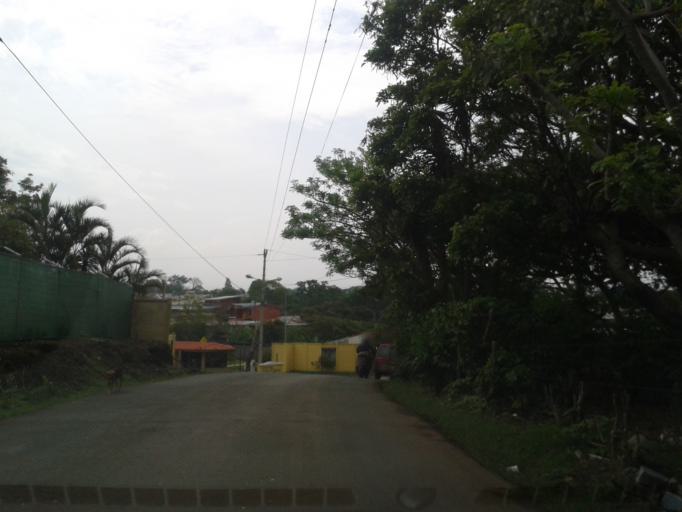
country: CR
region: Heredia
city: San Pablo
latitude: 9.9850
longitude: -84.1047
